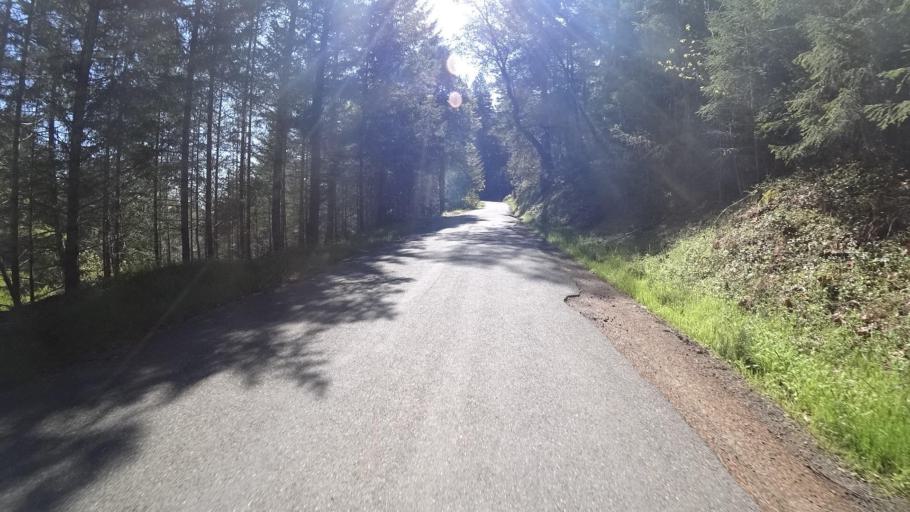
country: US
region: California
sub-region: Humboldt County
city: Redway
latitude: 40.0767
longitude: -123.6551
